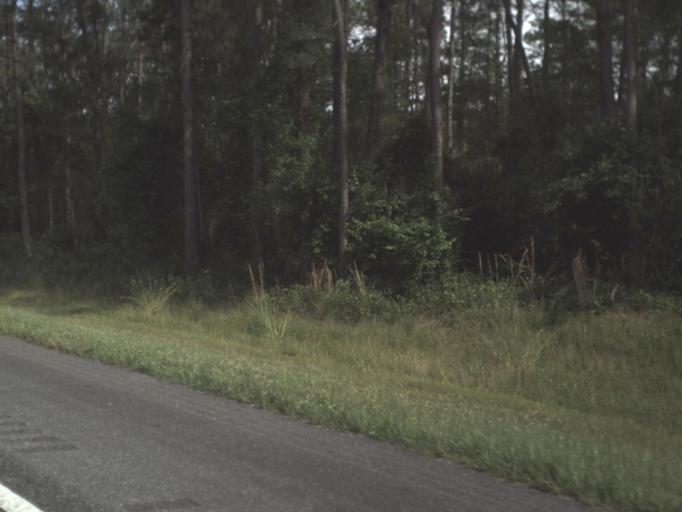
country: US
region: Florida
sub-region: Union County
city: Lake Butler
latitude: 30.2542
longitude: -82.3794
